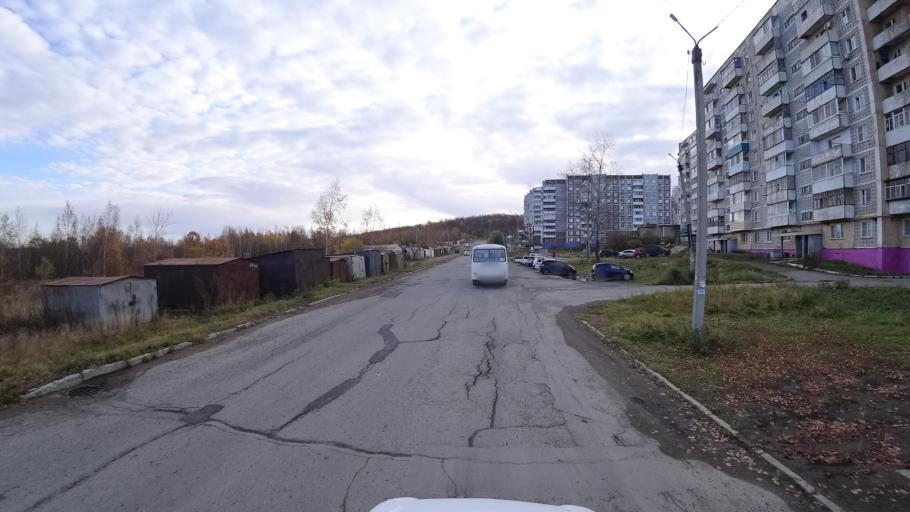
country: RU
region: Khabarovsk Krai
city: Amursk
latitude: 50.2491
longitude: 136.9182
